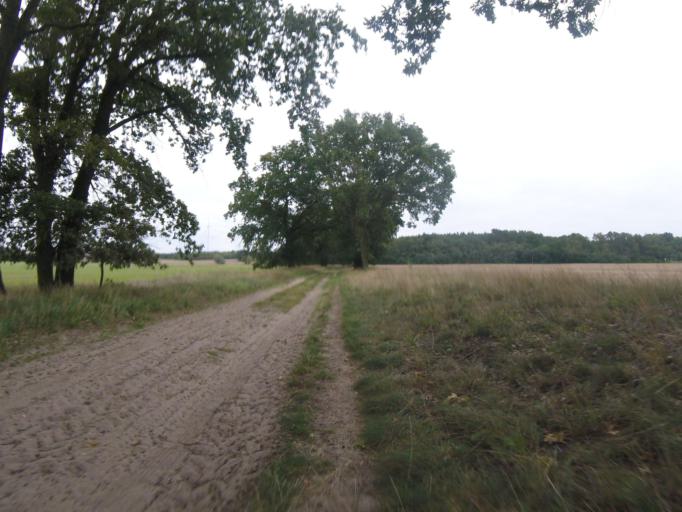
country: DE
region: Brandenburg
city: Mittenwalde
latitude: 52.2523
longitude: 13.5690
